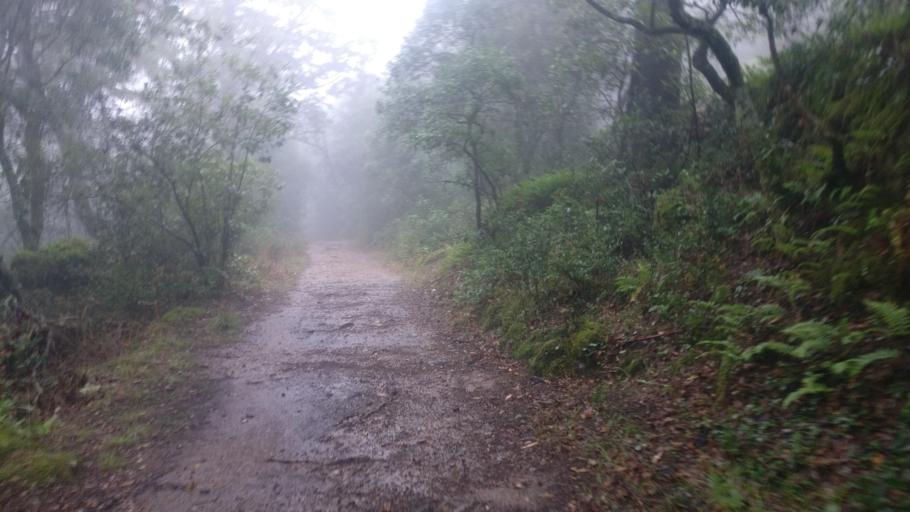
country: PT
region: Aveiro
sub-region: Mealhada
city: Pampilhosa do Botao
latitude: 40.3760
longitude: -8.3714
